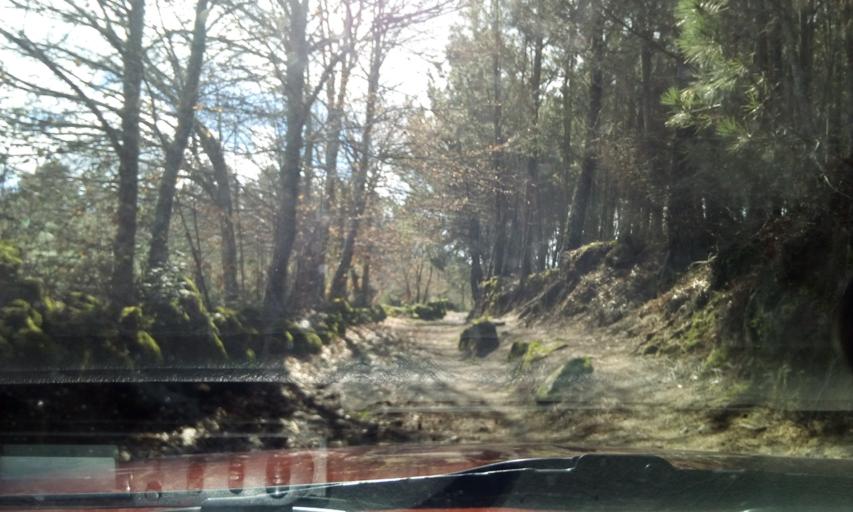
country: PT
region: Guarda
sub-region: Fornos de Algodres
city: Fornos de Algodres
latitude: 40.6523
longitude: -7.5130
